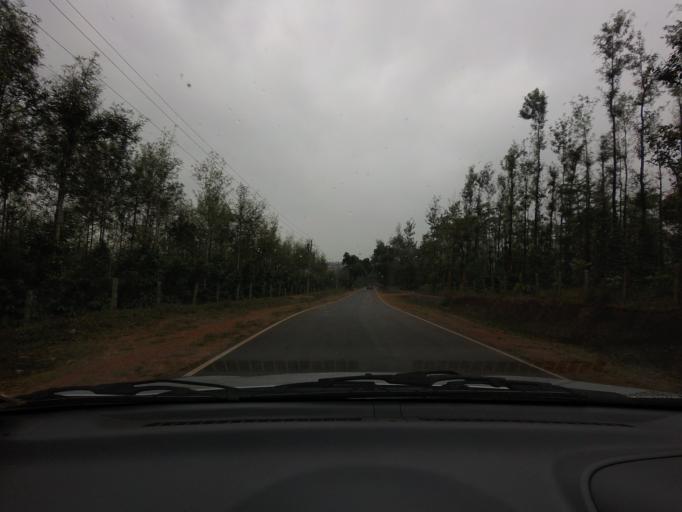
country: IN
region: Karnataka
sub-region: Hassan
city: Sakleshpur
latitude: 12.9902
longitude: 75.7111
